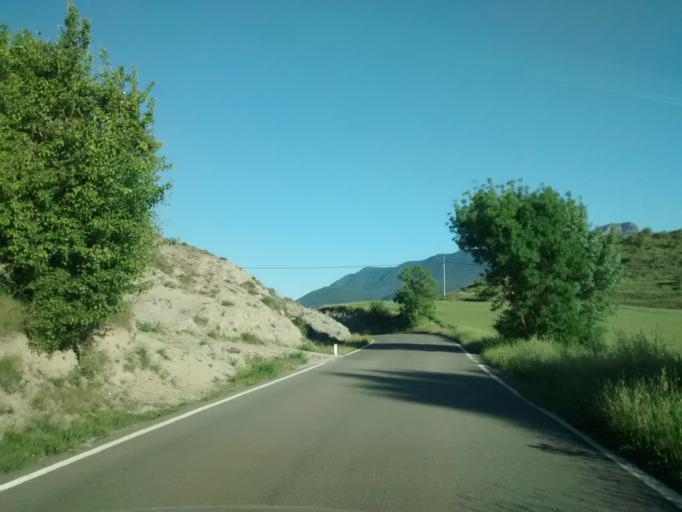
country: ES
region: Aragon
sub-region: Provincia de Huesca
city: Jaca
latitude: 42.5754
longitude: -0.5652
